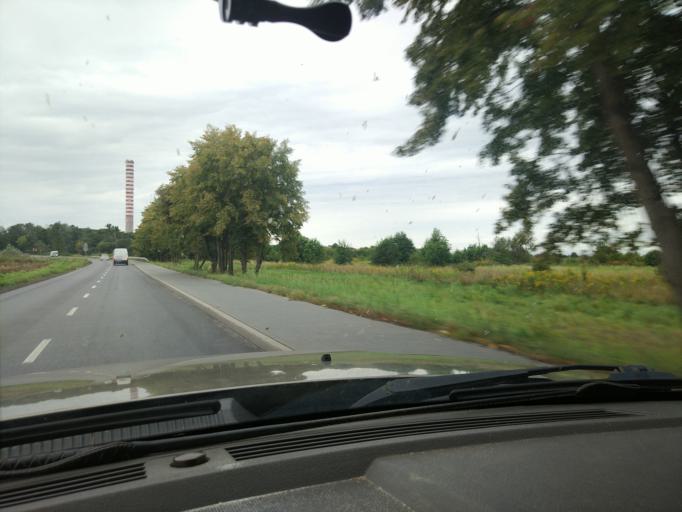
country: PL
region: Masovian Voivodeship
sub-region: Powiat warszawski zachodni
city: Ozarow Mazowiecki
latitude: 52.1871
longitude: 20.7518
